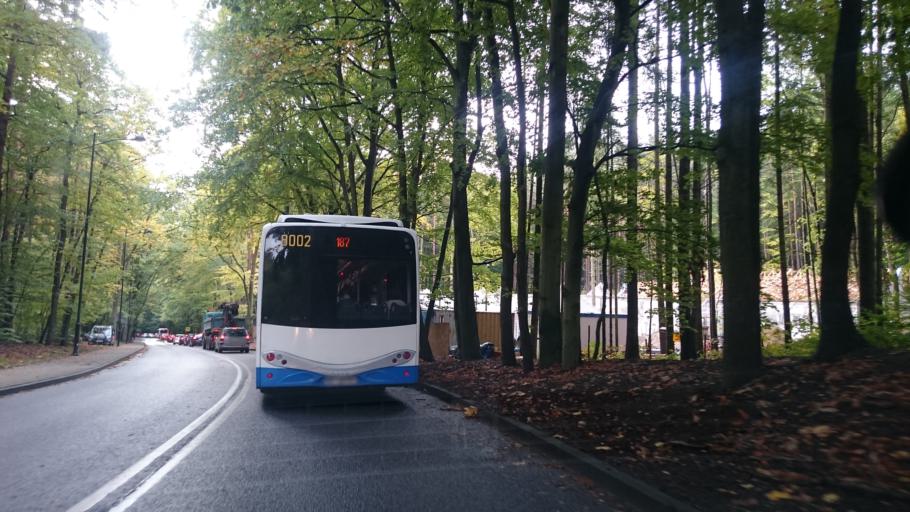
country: PL
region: Pomeranian Voivodeship
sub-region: Sopot
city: Sopot
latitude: 54.4537
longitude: 18.5397
